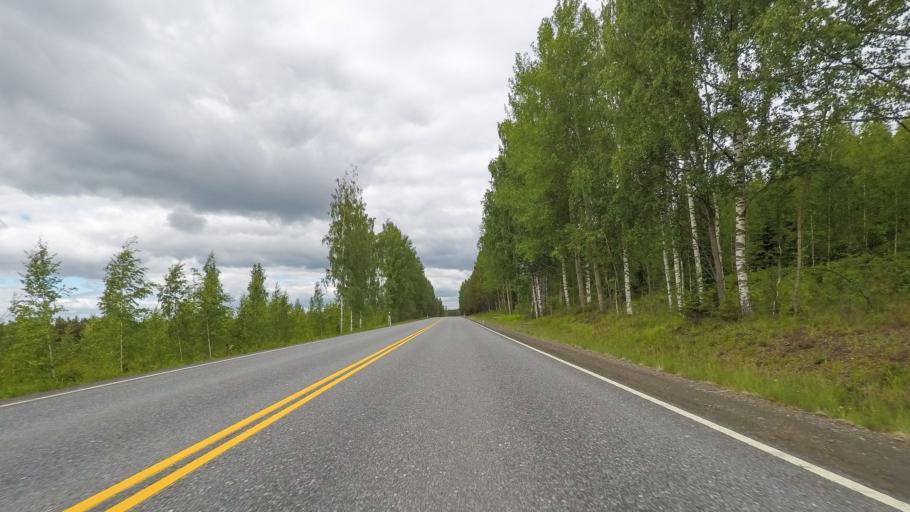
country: FI
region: Paijanne Tavastia
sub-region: Lahti
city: Hartola
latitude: 61.6527
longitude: 26.0282
